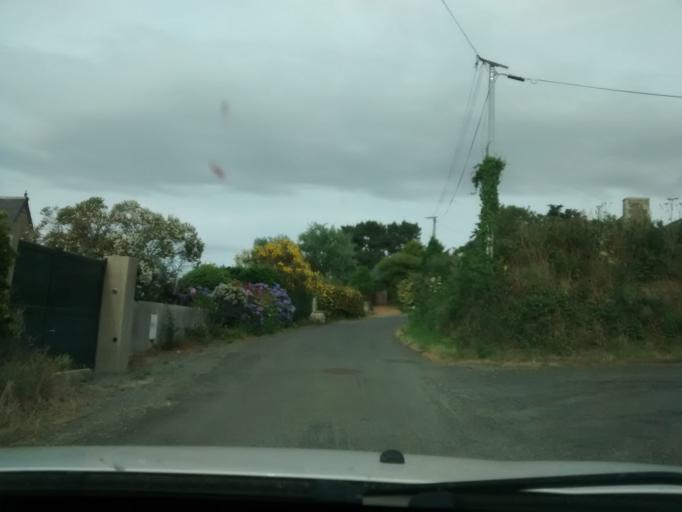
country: FR
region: Brittany
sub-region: Departement des Cotes-d'Armor
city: Penvenan
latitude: 48.8362
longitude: -3.2764
